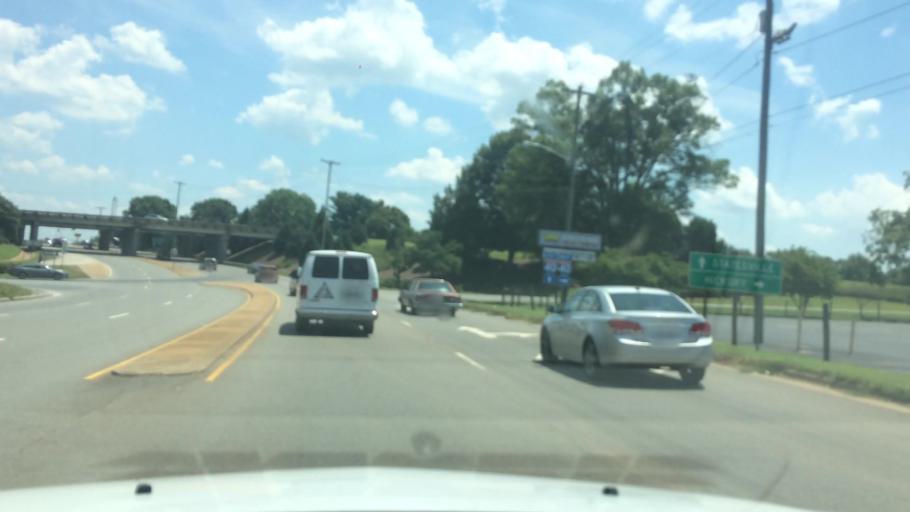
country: US
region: North Carolina
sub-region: Iredell County
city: Statesville
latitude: 35.7949
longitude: -80.9376
